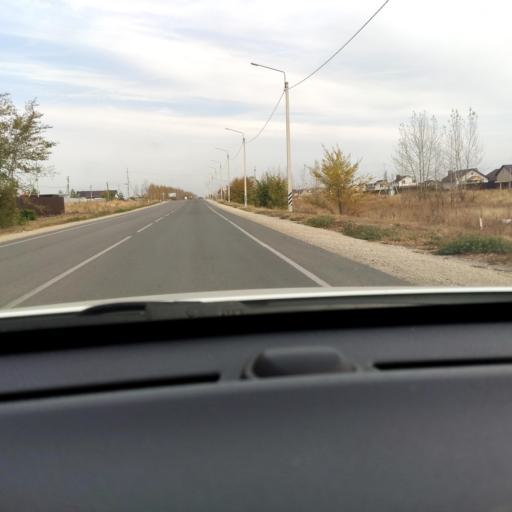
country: RU
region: Voronezj
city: Novaya Usman'
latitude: 51.6628
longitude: 39.4455
